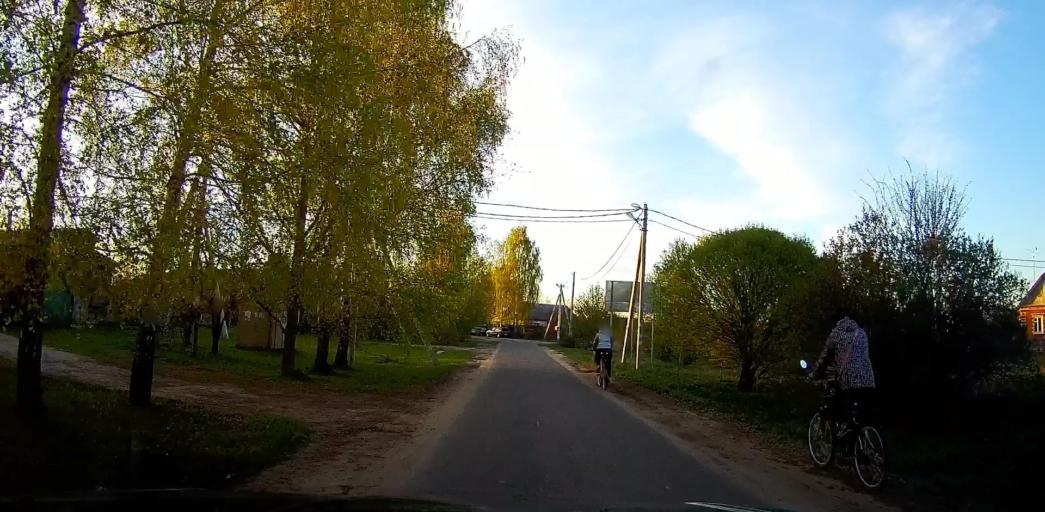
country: RU
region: Moskovskaya
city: Peski
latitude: 55.2091
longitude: 38.7392
